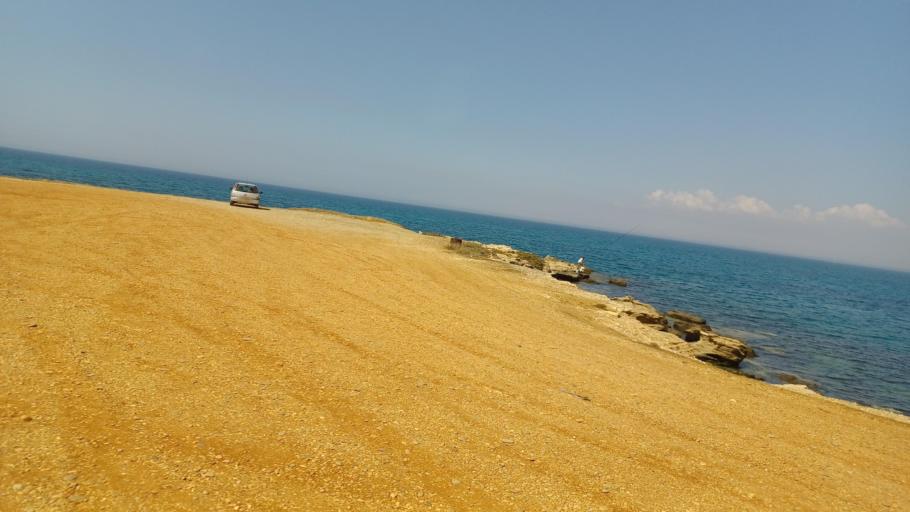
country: CY
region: Larnaka
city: Xylotymbou
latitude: 34.9776
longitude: 33.7833
